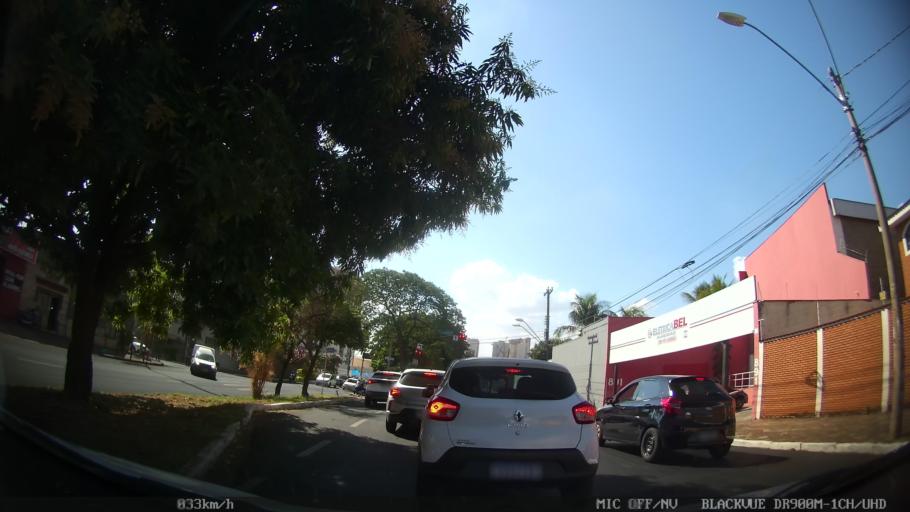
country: BR
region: Sao Paulo
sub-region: Ribeirao Preto
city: Ribeirao Preto
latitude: -21.1865
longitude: -47.8197
